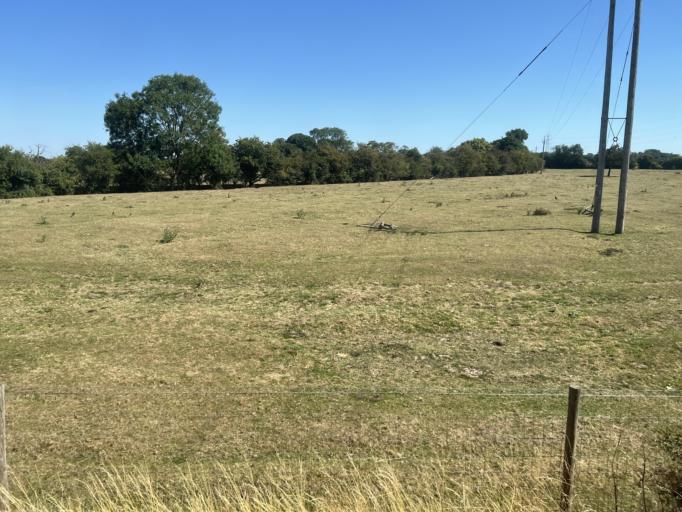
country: GB
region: England
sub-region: Lincolnshire
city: Wainfleet All Saints
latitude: 53.1212
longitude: 0.2019
